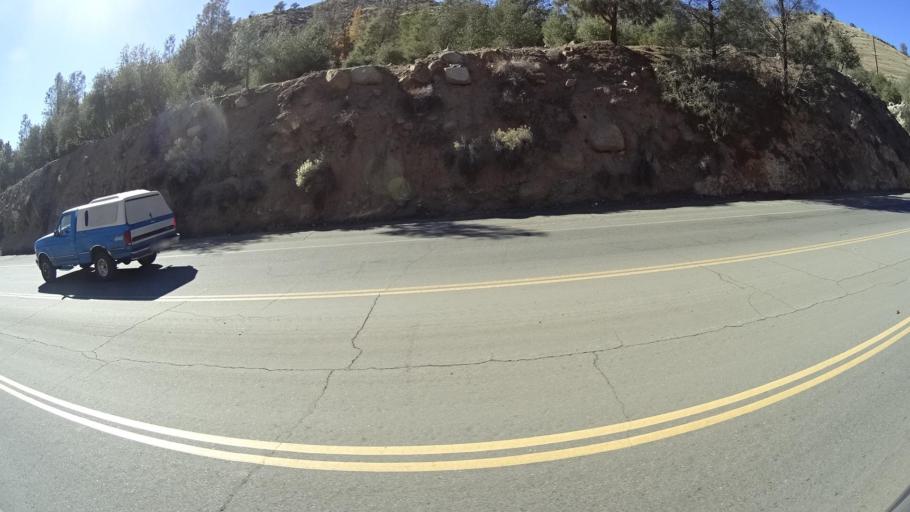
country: US
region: California
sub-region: Kern County
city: Kernville
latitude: 35.7493
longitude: -118.4224
